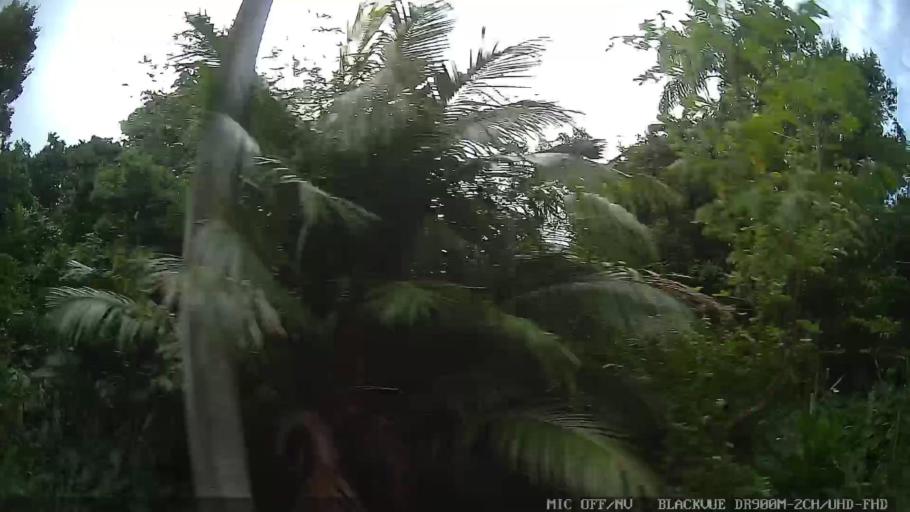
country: BR
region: Sao Paulo
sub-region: Iguape
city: Iguape
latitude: -24.6546
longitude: -47.4061
